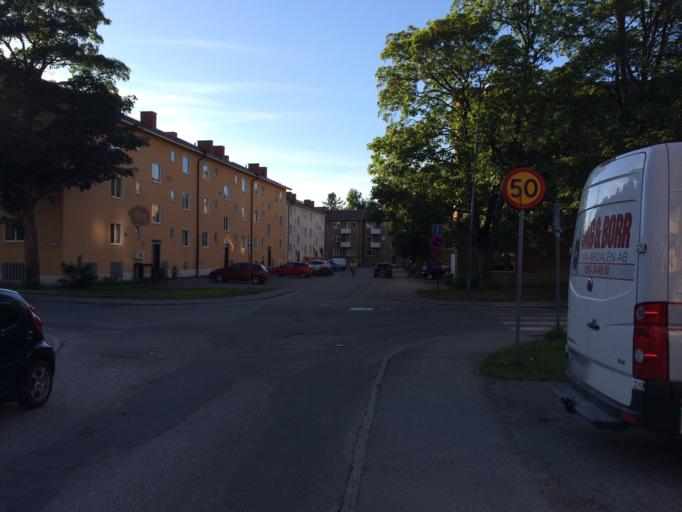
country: SE
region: Stockholm
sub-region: Huddinge Kommun
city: Segeltorp
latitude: 59.2959
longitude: 17.9724
